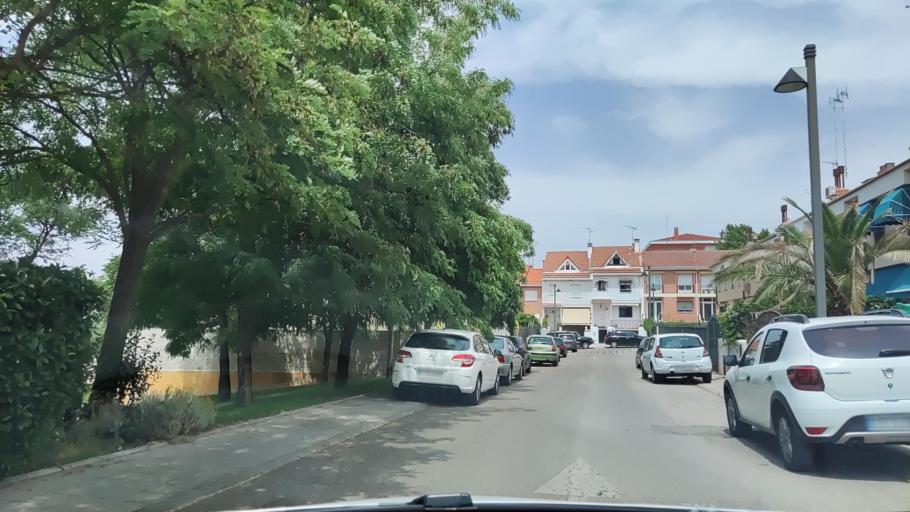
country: ES
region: Madrid
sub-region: Provincia de Madrid
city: Navalcarnero
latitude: 40.2868
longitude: -4.0237
